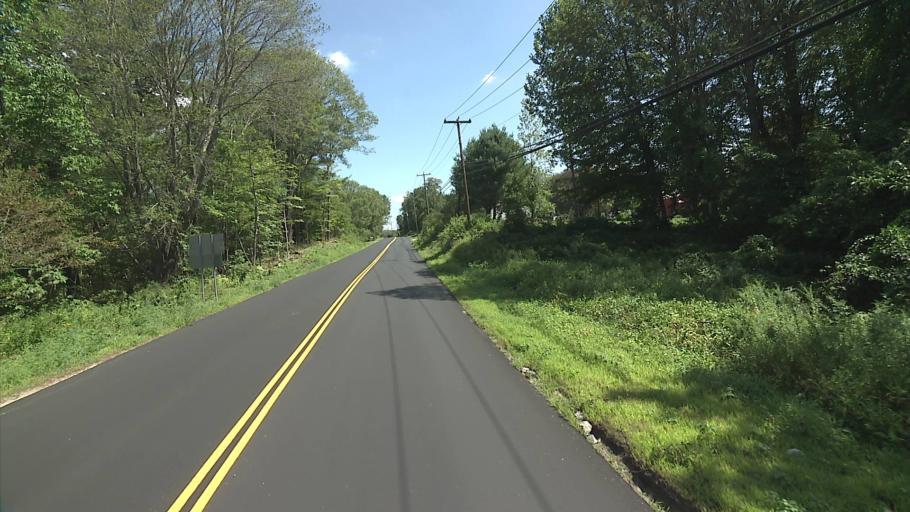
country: US
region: Connecticut
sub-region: Windham County
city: South Woodstock
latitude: 41.9301
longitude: -72.0823
